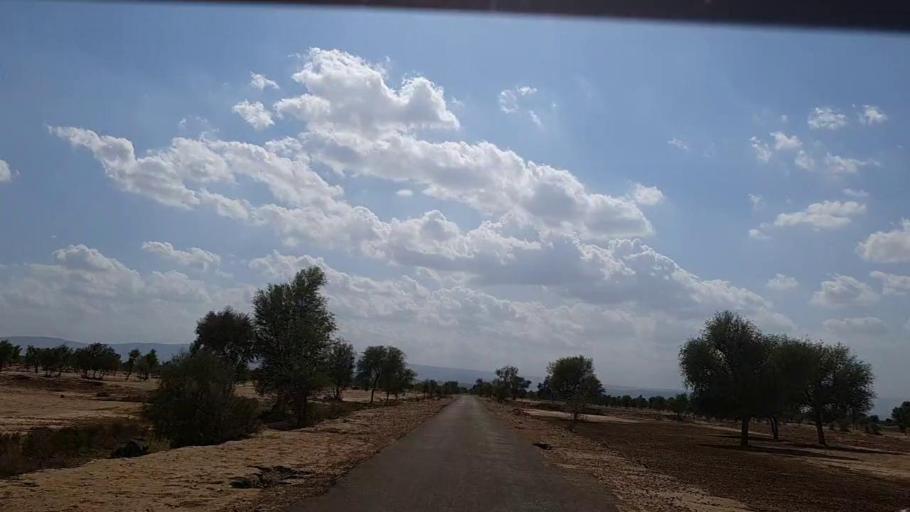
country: PK
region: Sindh
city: Johi
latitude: 26.5208
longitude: 67.4696
